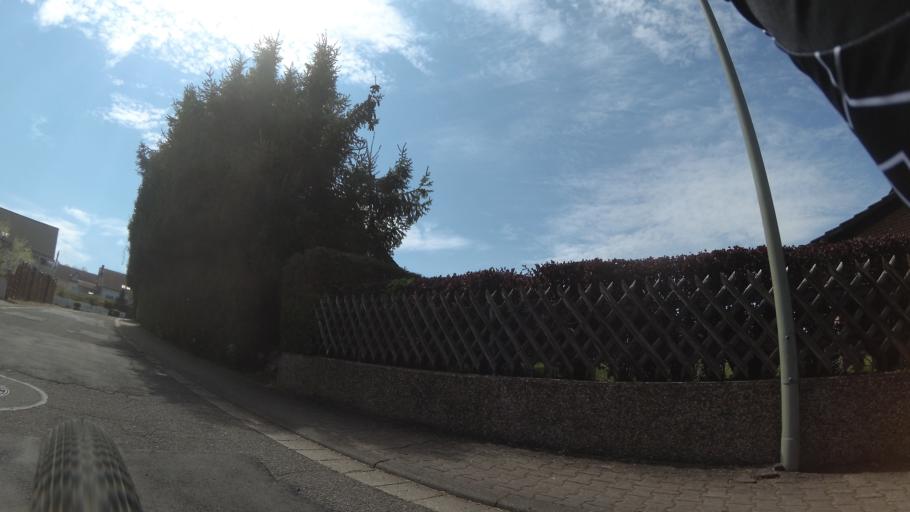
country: DE
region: Rheinland-Pfalz
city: Brucken
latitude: 49.4281
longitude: 7.3569
